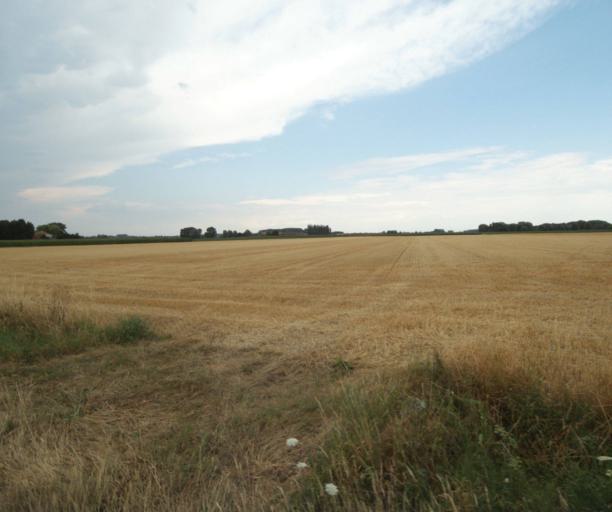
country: FR
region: Nord-Pas-de-Calais
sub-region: Departement du Nord
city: Deulemont
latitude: 50.7345
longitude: 2.9598
